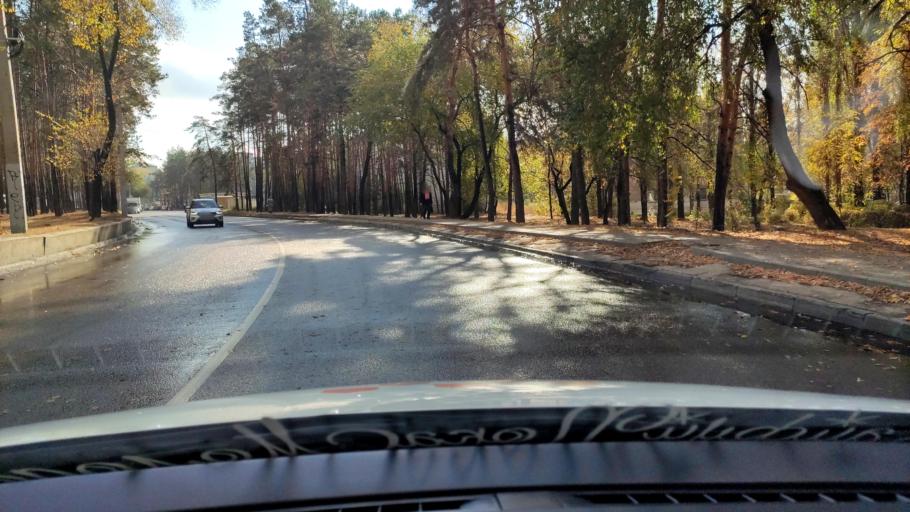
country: RU
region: Voronezj
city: Pridonskoy
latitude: 51.6851
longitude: 39.0808
